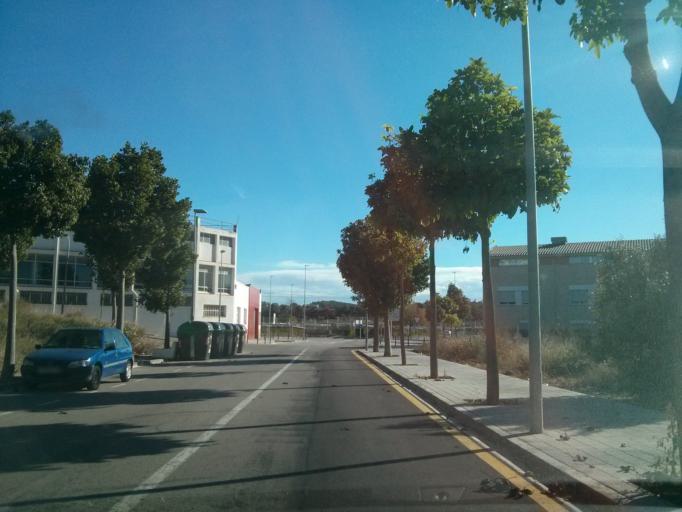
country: ES
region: Catalonia
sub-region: Provincia de Tarragona
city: El Vendrell
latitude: 41.2127
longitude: 1.5336
